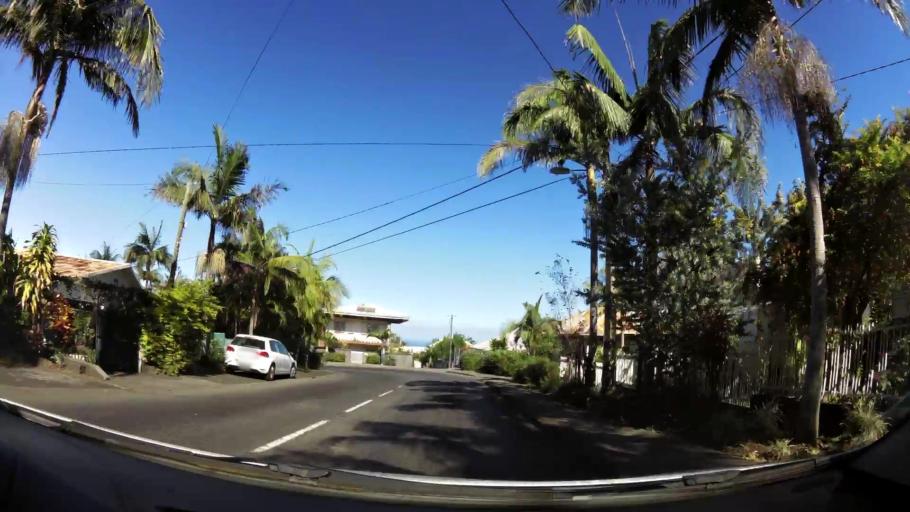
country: RE
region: Reunion
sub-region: Reunion
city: Le Tampon
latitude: -21.2816
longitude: 55.5241
